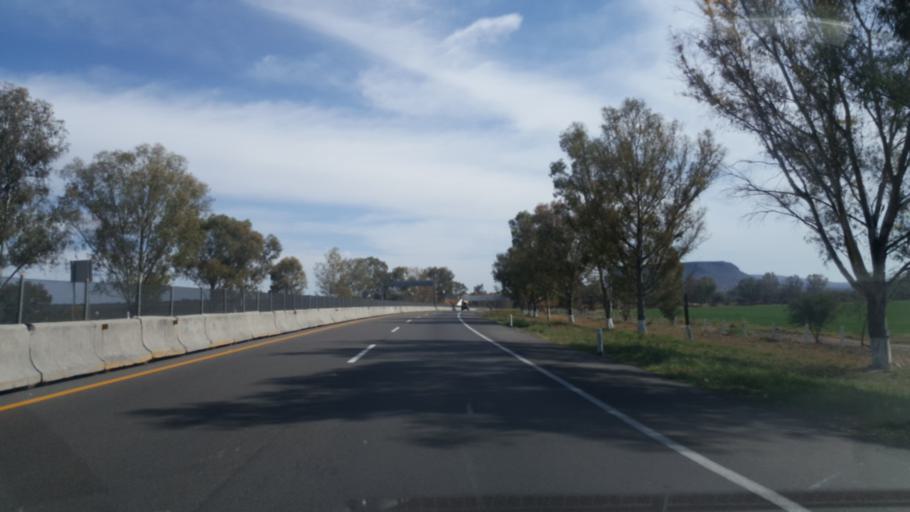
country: MX
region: Jalisco
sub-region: Lagos de Moreno
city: Cristeros [Fraccionamiento]
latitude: 21.3157
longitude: -102.0386
